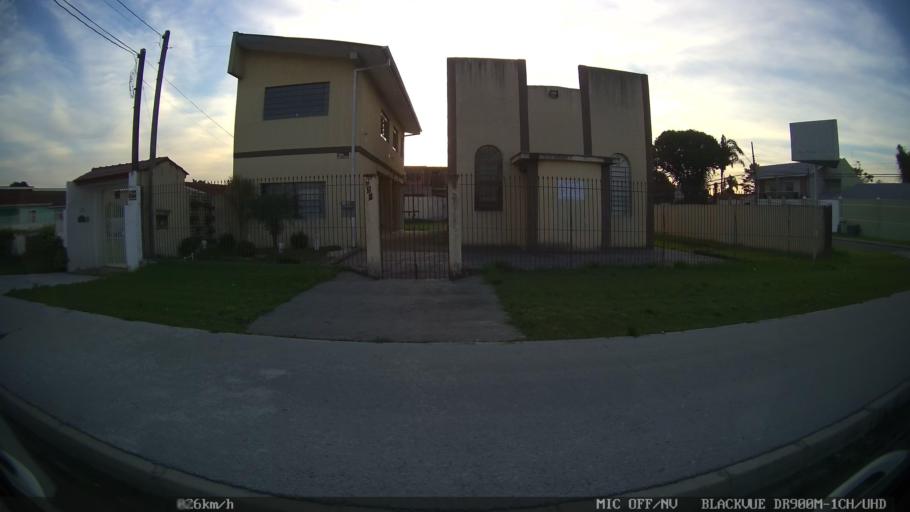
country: BR
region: Parana
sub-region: Pinhais
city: Pinhais
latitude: -25.4529
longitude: -49.1815
